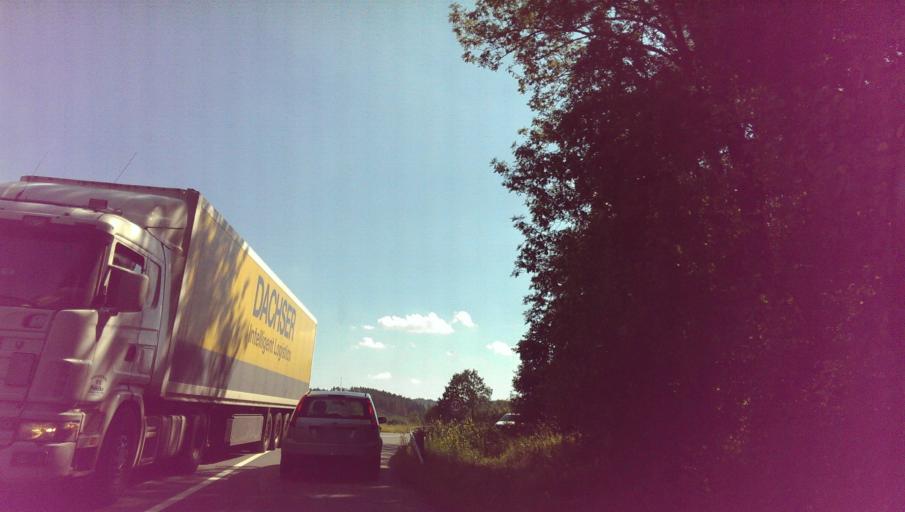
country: CZ
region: Zlin
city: Kelc
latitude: 49.4498
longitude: 17.8719
